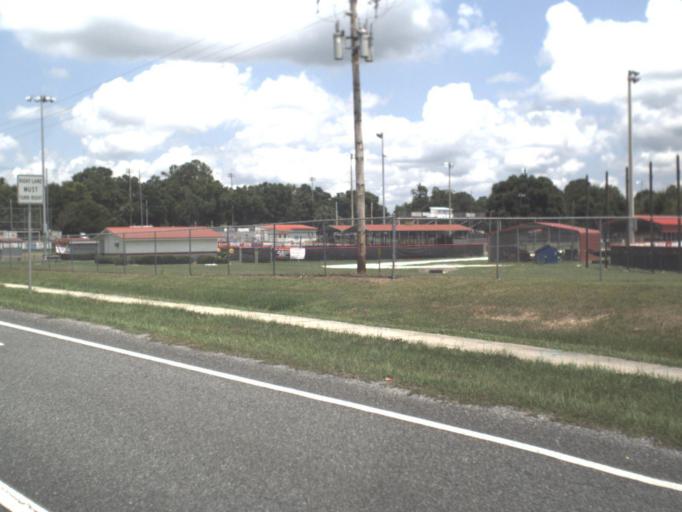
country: US
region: Florida
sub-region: Alachua County
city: High Springs
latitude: 29.8038
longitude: -82.5236
